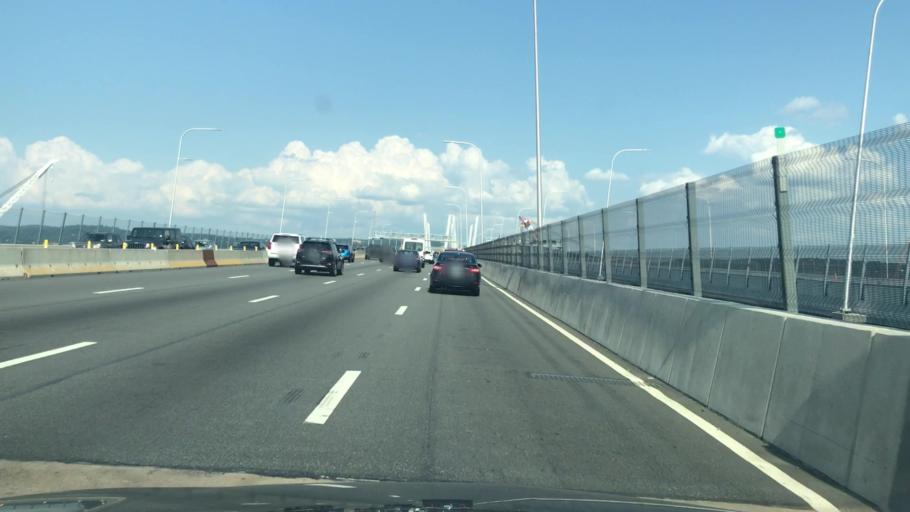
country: US
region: New York
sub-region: Rockland County
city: South Nyack
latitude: 41.0717
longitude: -73.9034
